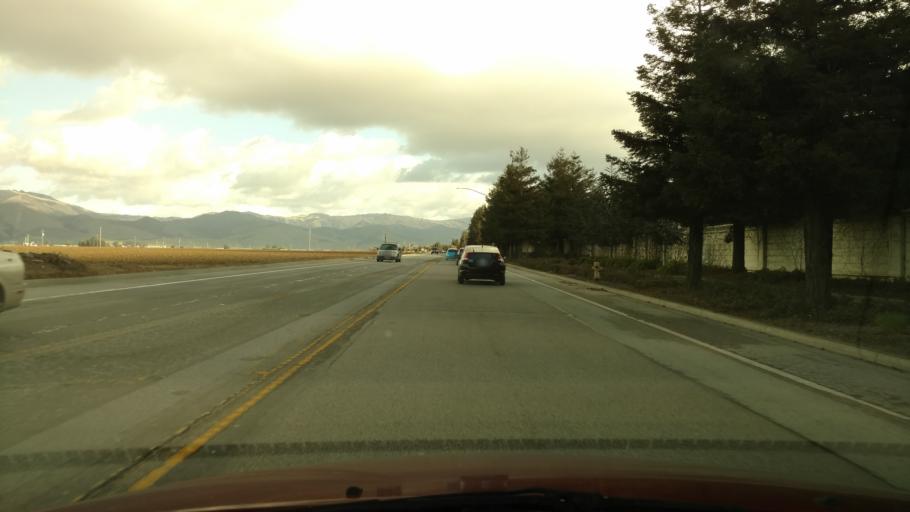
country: US
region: California
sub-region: Monterey County
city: Boronda
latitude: 36.7168
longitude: -121.6422
